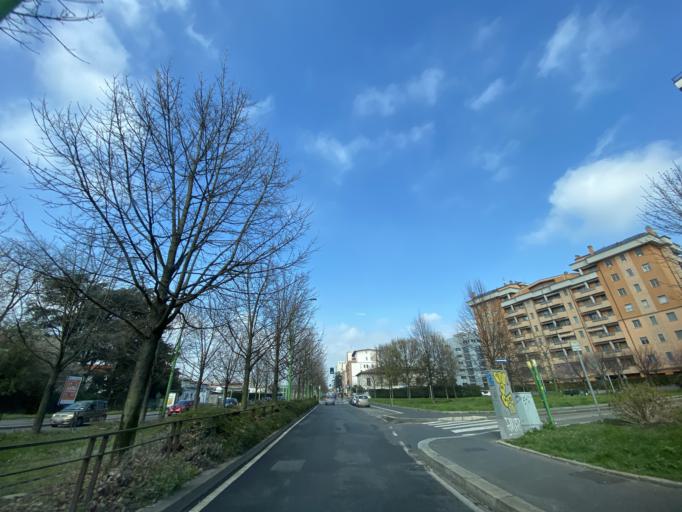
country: IT
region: Lombardy
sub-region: Citta metropolitana di Milano
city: Bresso
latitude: 45.5224
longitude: 9.1923
